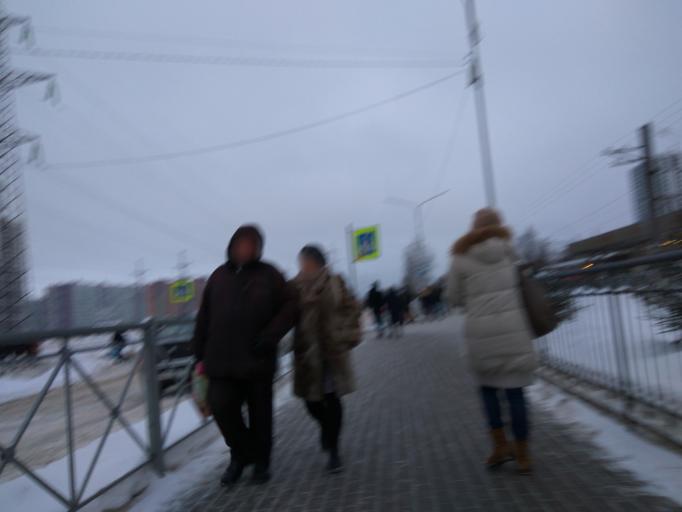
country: RU
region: Leningrad
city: Murino
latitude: 60.0503
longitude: 30.4416
